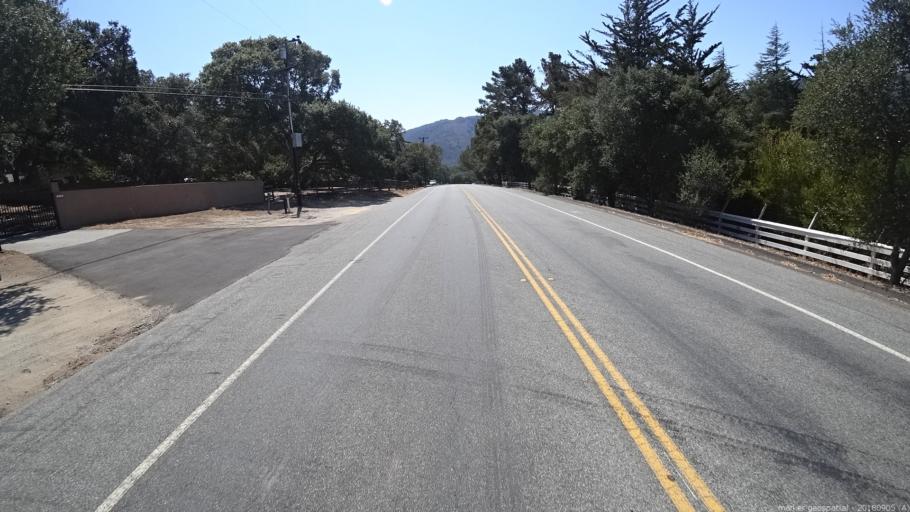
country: US
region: California
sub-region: Monterey County
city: Carmel Valley Village
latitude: 36.5050
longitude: -121.7523
